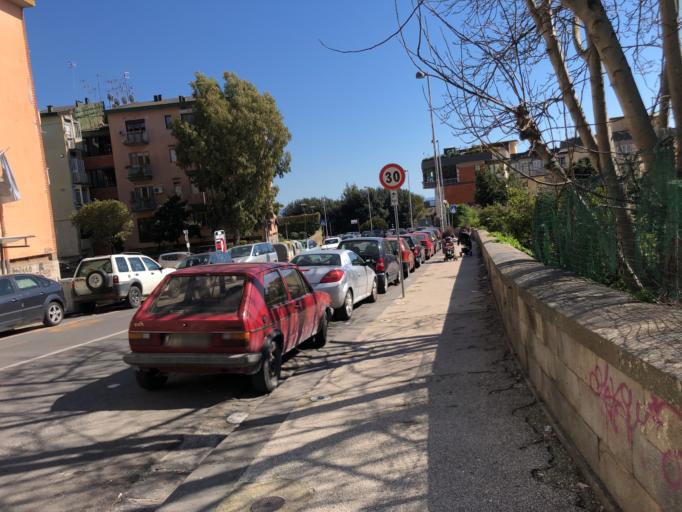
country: IT
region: Campania
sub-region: Provincia di Napoli
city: Napoli
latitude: 40.8598
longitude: 14.2237
